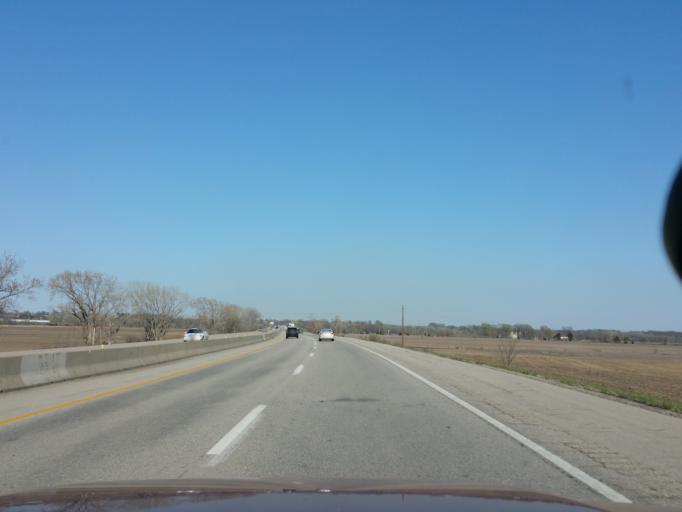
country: US
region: Kansas
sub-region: Douglas County
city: Lawrence
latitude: 38.9939
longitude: -95.2003
